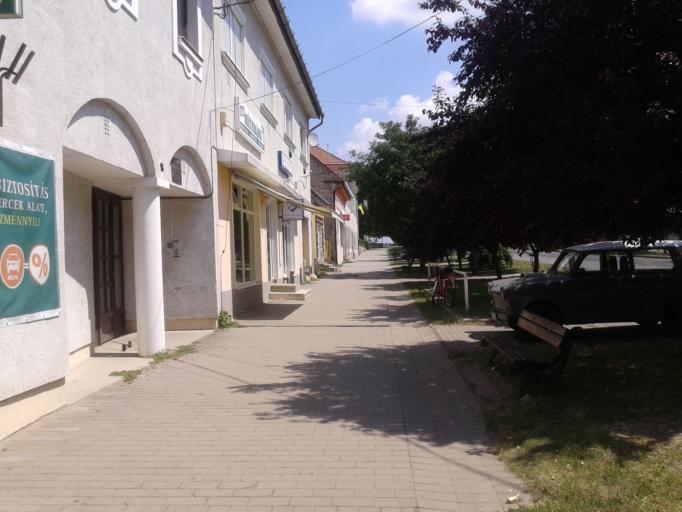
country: HU
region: Fejer
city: Bicske
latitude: 47.4903
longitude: 18.6337
